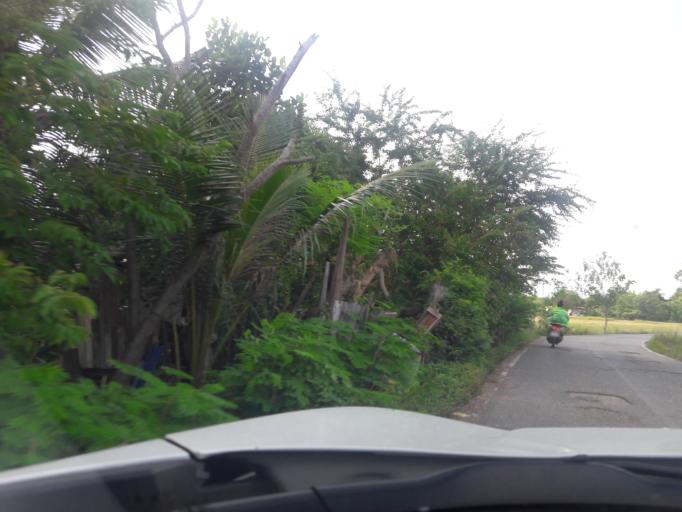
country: TH
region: Lop Buri
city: Ban Mi
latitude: 15.0538
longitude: 100.5417
